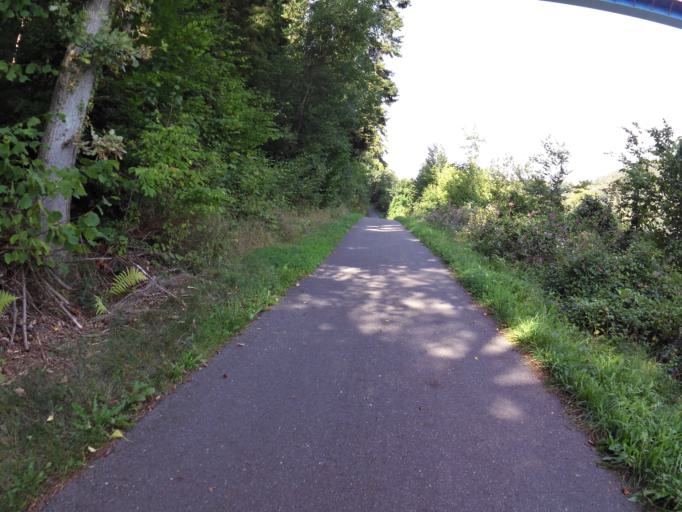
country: DE
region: Baden-Wuerttemberg
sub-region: Karlsruhe Region
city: Horb am Neckar
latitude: 48.4470
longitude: 8.7674
